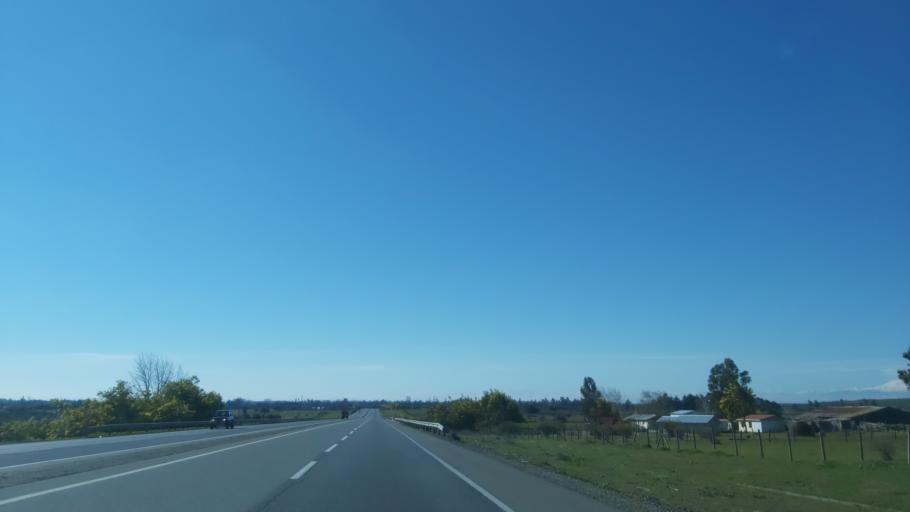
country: CL
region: Biobio
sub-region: Provincia de Nuble
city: Bulnes
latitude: -36.6585
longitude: -72.2514
